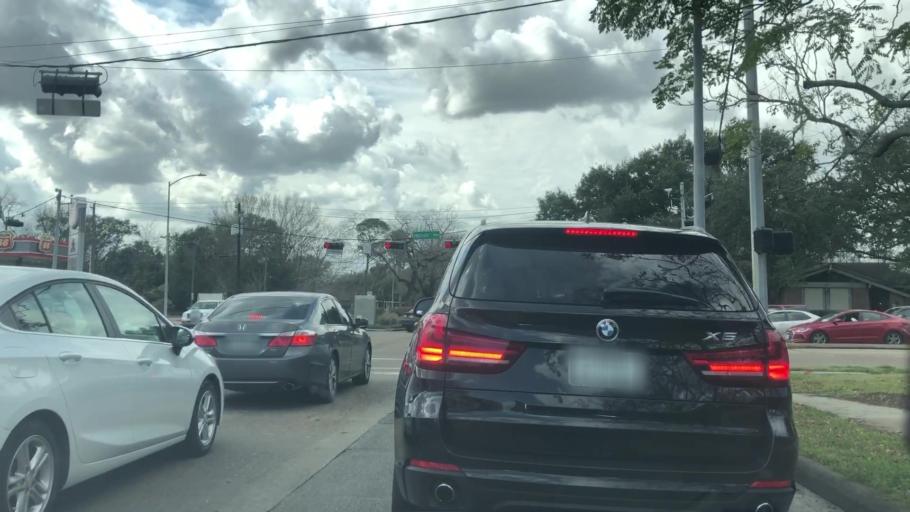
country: US
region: Texas
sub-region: Harris County
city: Bellaire
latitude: 29.6884
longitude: -95.4921
